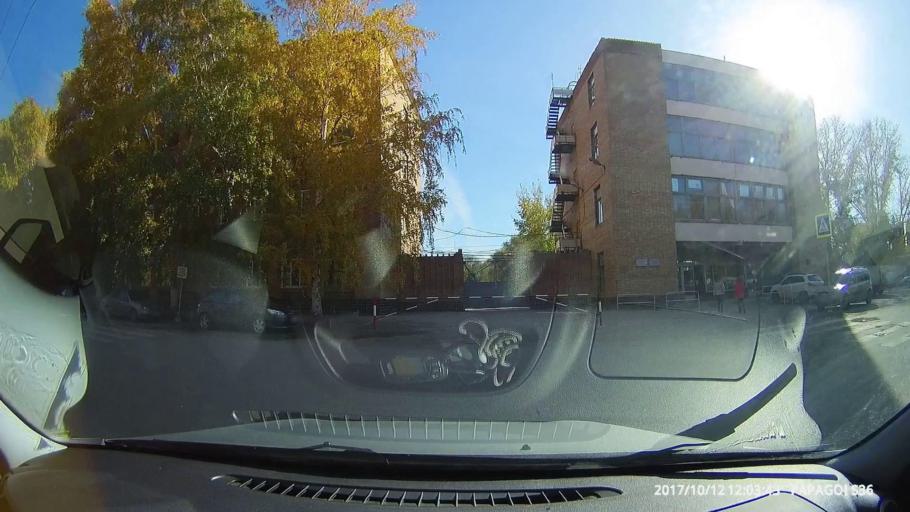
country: RU
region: Samara
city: Chapayevsk
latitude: 52.9764
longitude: 49.7161
